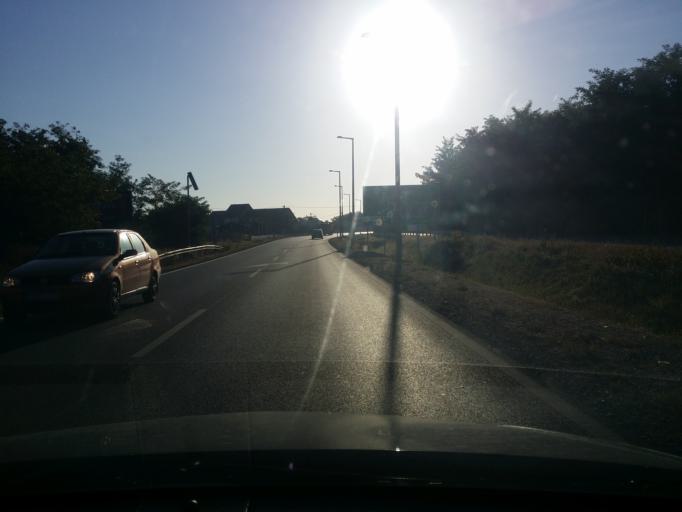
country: HU
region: Bacs-Kiskun
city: Kecskemet
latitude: 46.9061
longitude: 19.7427
